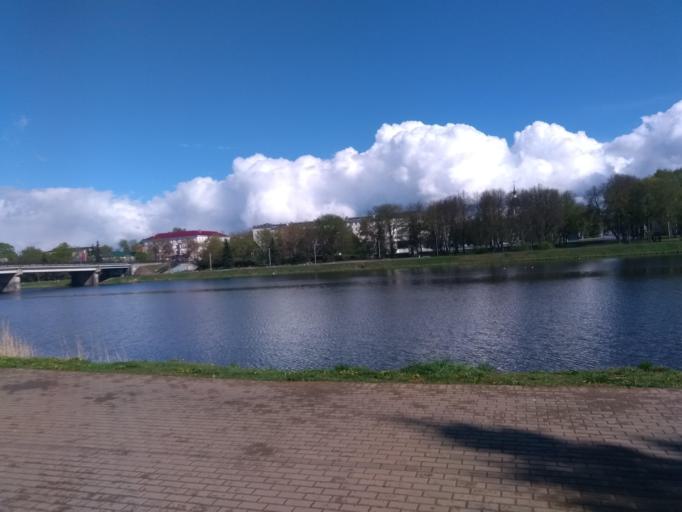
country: RU
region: Pskov
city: Velikiye Luki
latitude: 56.3452
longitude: 30.5120
